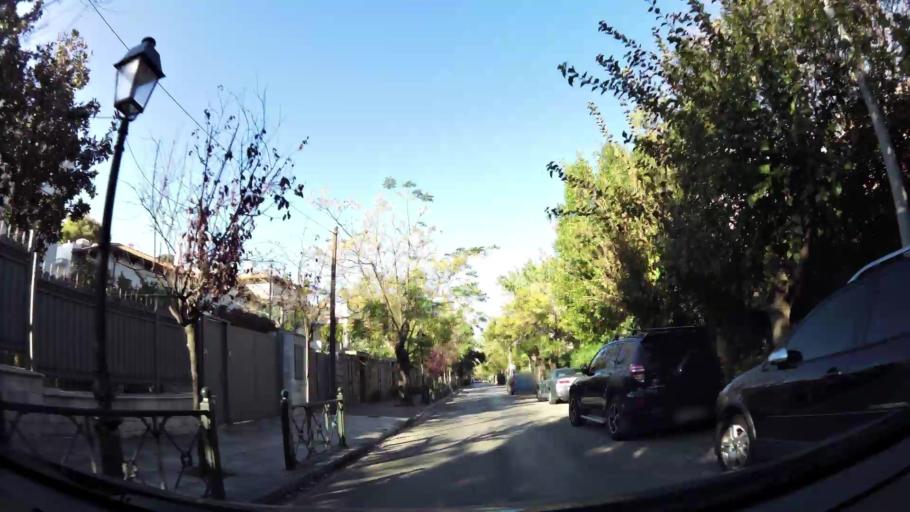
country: GR
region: Attica
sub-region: Nomarchia Athinas
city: Kifisia
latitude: 38.0757
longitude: 23.8145
